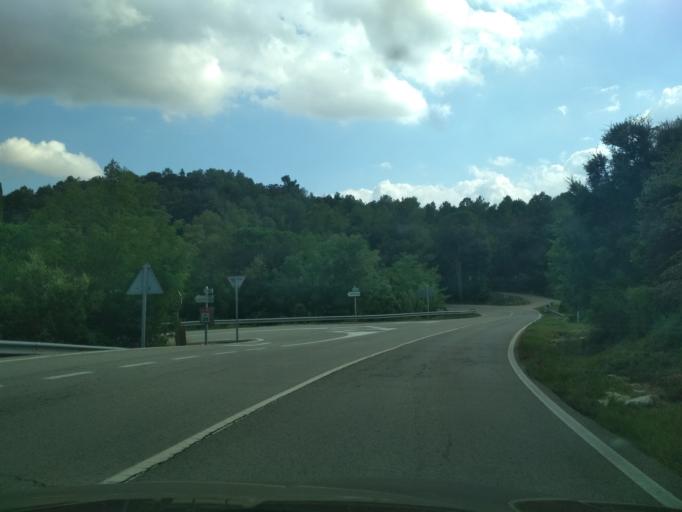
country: ES
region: Catalonia
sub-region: Provincia de Barcelona
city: Sant Feliu de Codines
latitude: 41.7078
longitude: 2.1562
